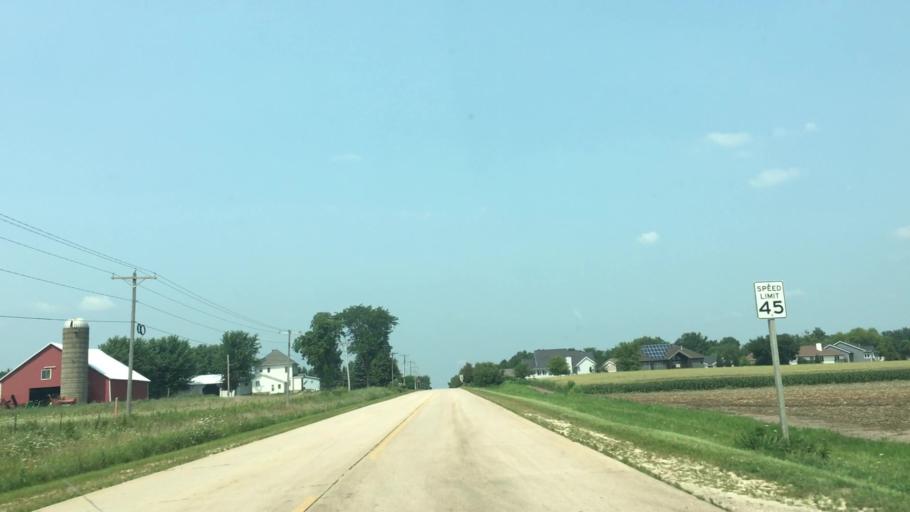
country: US
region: Iowa
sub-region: Fayette County
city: Oelwein
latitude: 42.6725
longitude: -91.8937
